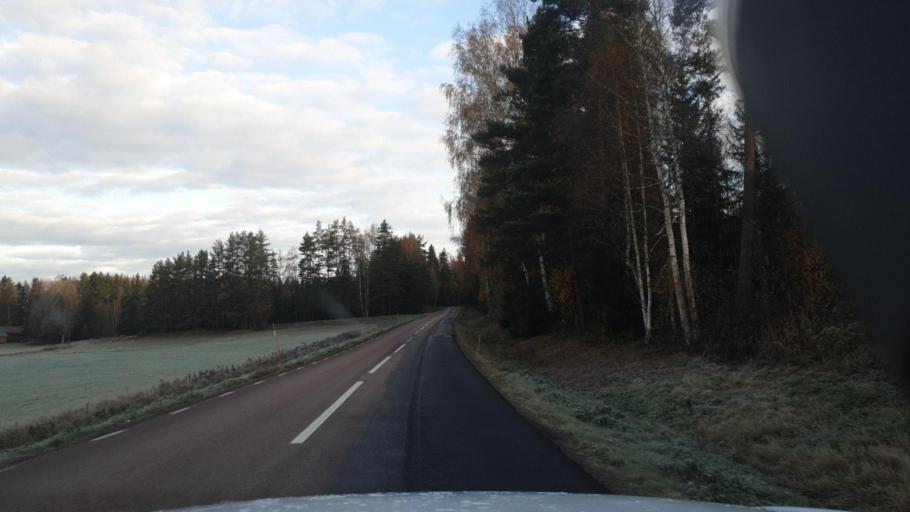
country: SE
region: Vaermland
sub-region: Eda Kommun
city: Amotfors
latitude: 59.7501
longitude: 12.2115
